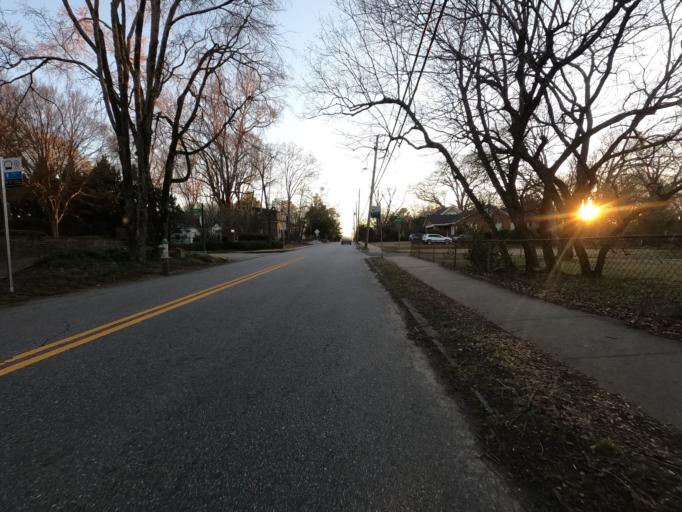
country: US
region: Georgia
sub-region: Clarke County
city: Athens
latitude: 33.9352
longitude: -83.3894
